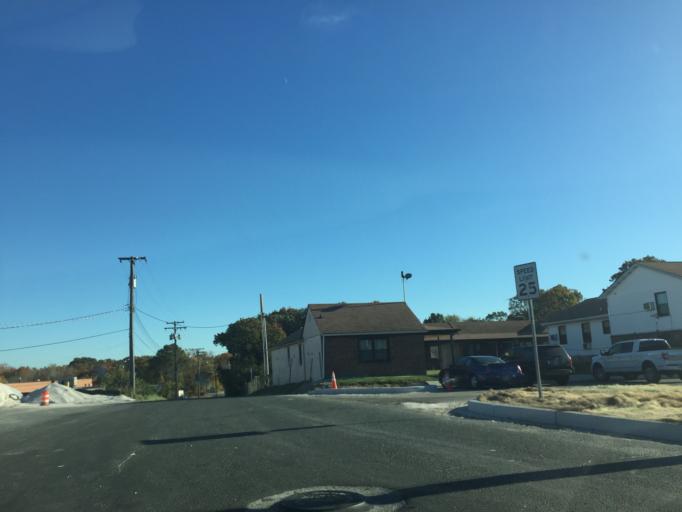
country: US
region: Maryland
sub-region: Baltimore County
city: Rosedale
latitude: 39.3213
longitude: -76.5064
